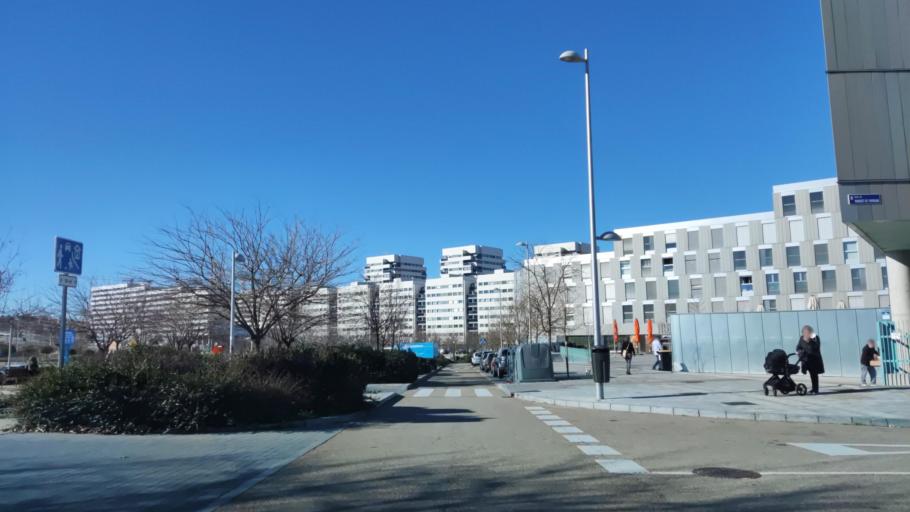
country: ES
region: Madrid
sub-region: Provincia de Madrid
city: Hortaleza
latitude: 40.4863
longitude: -3.6118
